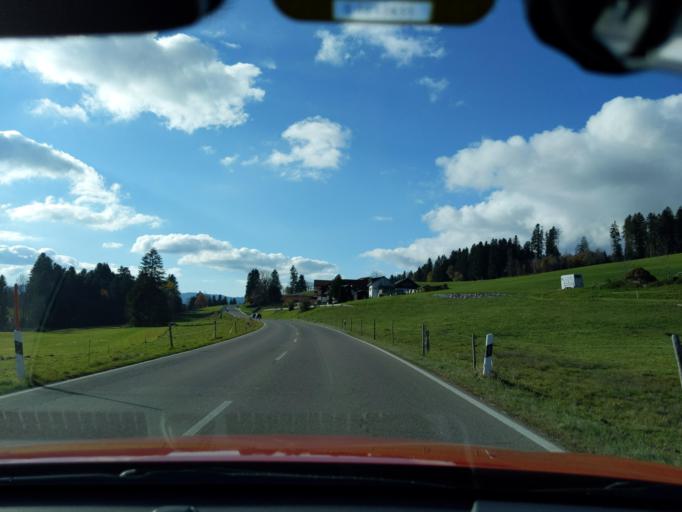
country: DE
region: Bavaria
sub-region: Swabia
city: Oberreute
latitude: 47.5691
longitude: 9.9387
